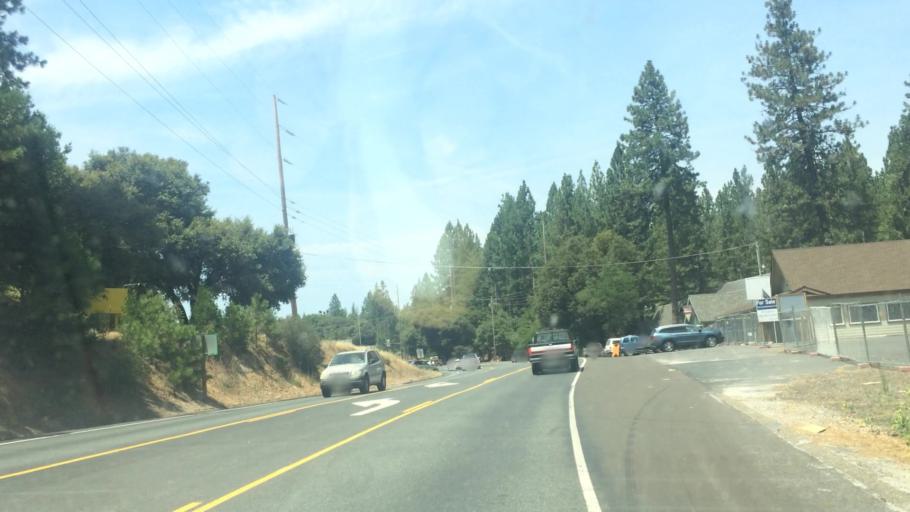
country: US
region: California
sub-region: Amador County
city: Pine Grove
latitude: 38.4111
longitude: -120.6525
